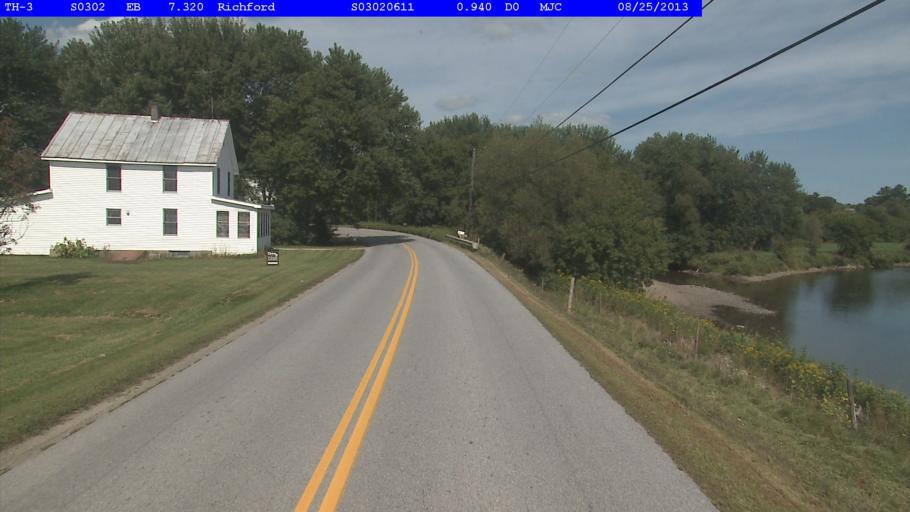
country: US
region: Vermont
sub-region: Franklin County
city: Richford
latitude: 44.9984
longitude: -72.6812
